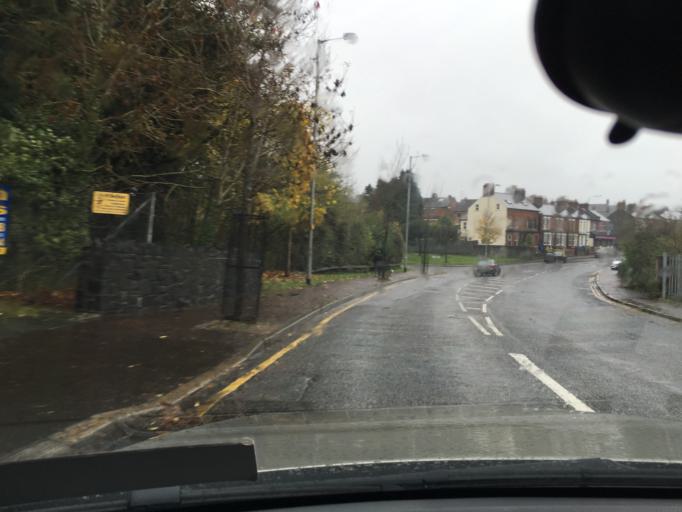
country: GB
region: Northern Ireland
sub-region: City of Belfast
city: Belfast
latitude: 54.6094
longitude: -5.9717
